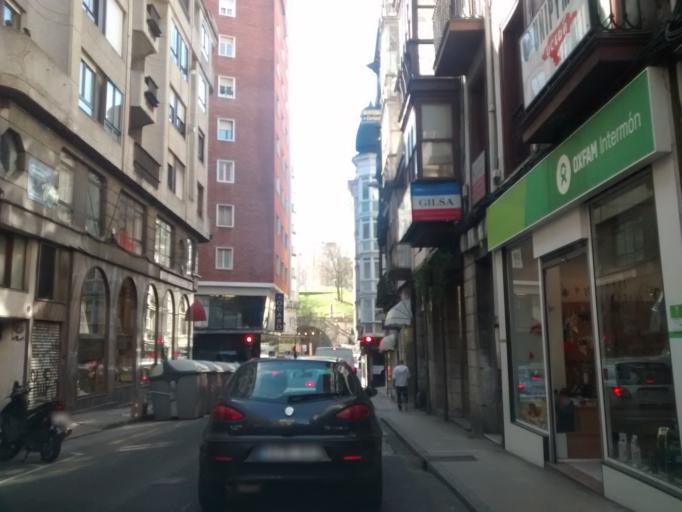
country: ES
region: Cantabria
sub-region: Provincia de Cantabria
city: Santander
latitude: 43.4626
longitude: -3.8116
